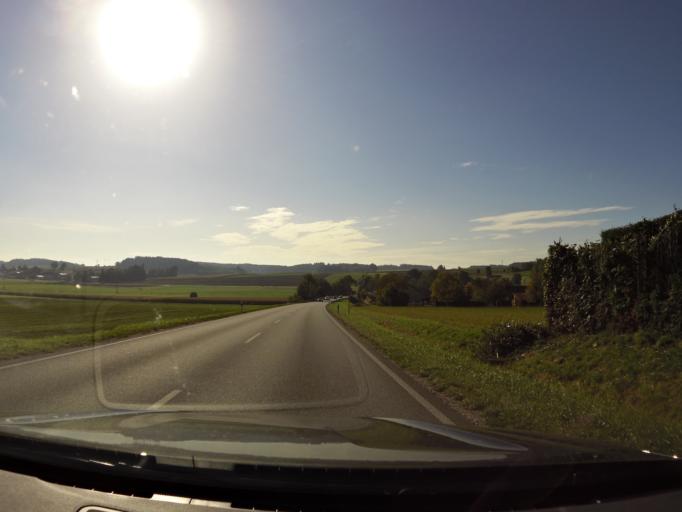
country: DE
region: Bavaria
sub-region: Lower Bavaria
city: Altfraunhofen
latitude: 48.4546
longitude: 12.1500
